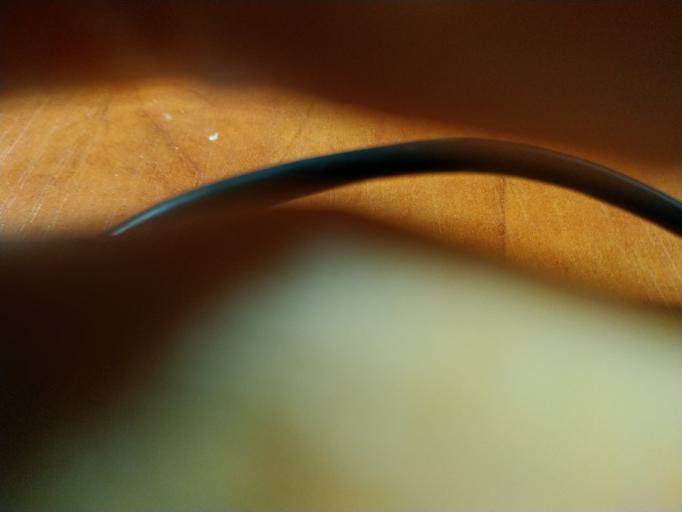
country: RU
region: Tverskaya
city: Likhoslavl'
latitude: 57.2756
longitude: 35.6172
